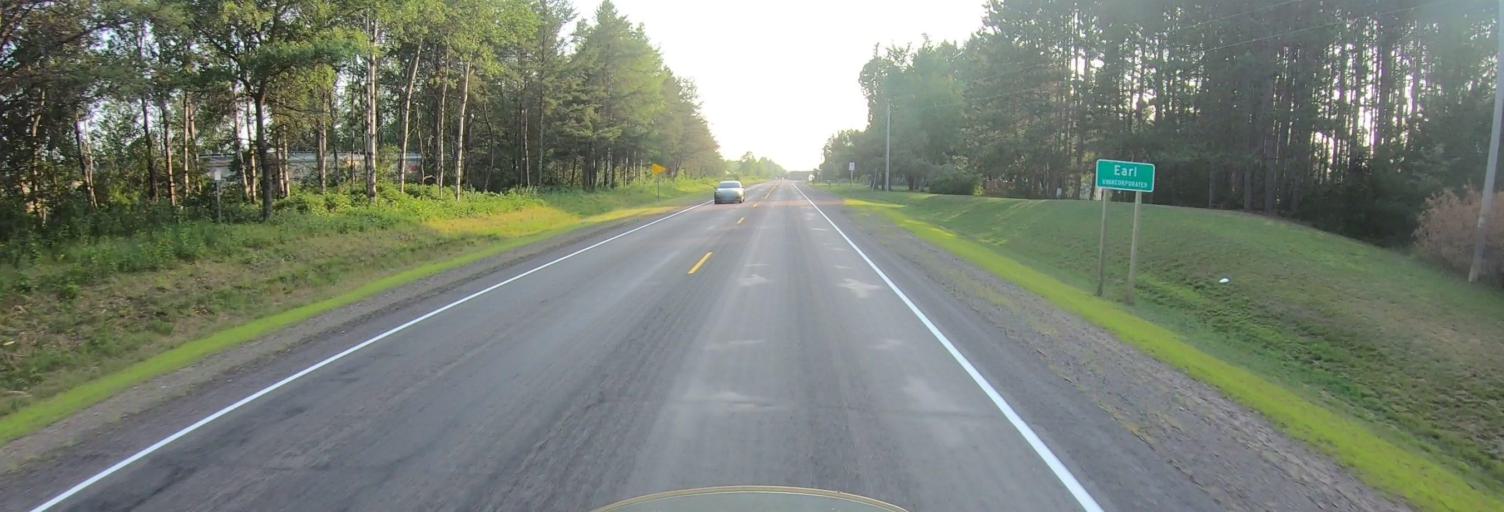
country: US
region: Wisconsin
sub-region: Washburn County
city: Spooner
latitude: 45.9138
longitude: -91.7568
